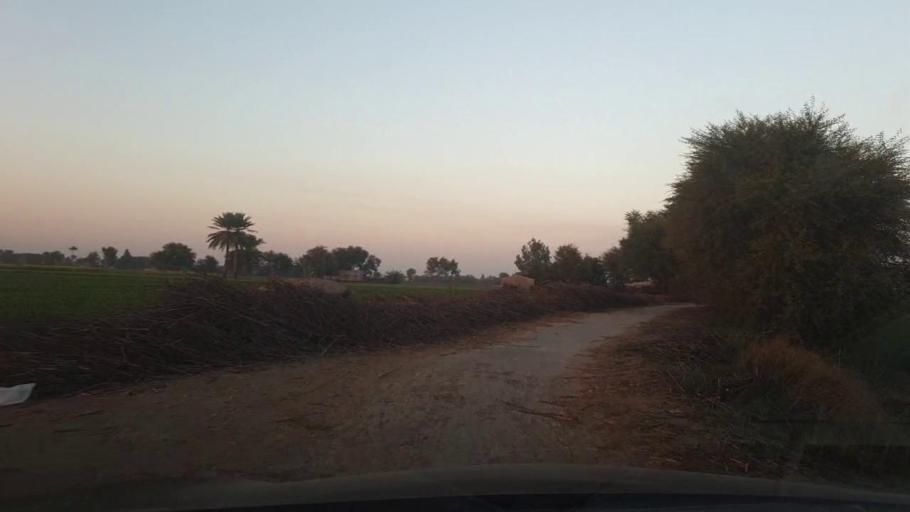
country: PK
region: Sindh
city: Ubauro
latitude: 28.1704
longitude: 69.6352
